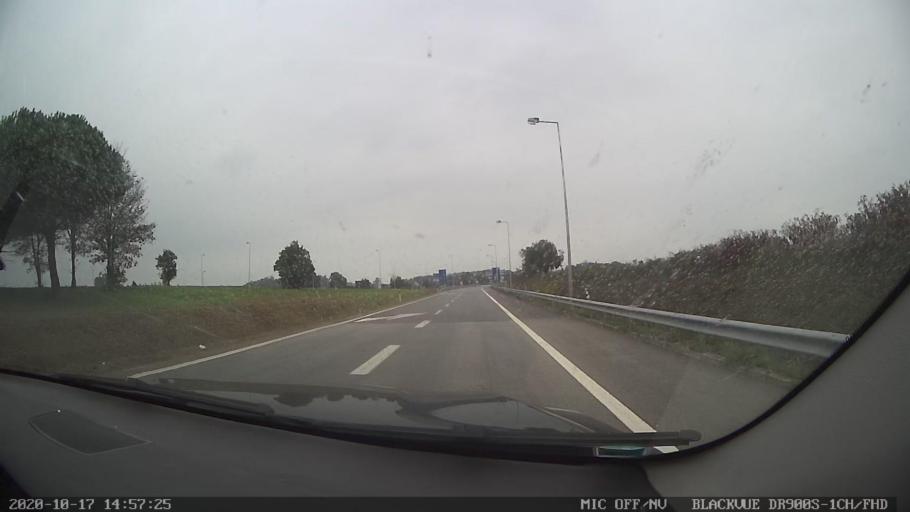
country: PT
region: Braga
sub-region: Esposende
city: Apulia
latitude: 41.4902
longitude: -8.7441
